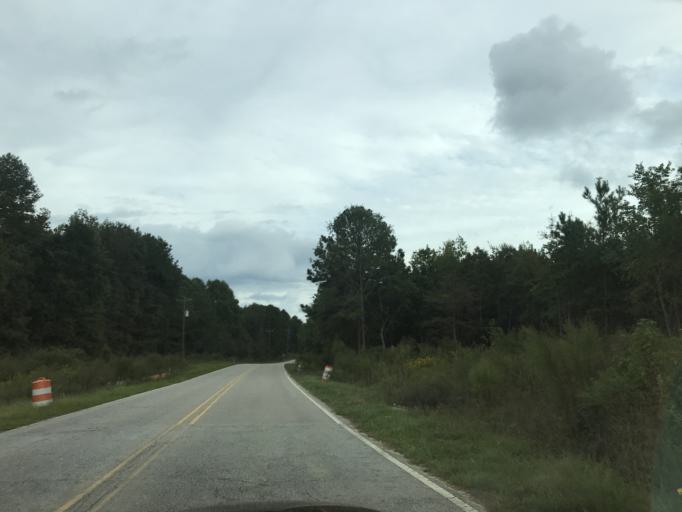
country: US
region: North Carolina
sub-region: Wake County
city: Rolesville
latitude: 35.9818
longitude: -78.3819
